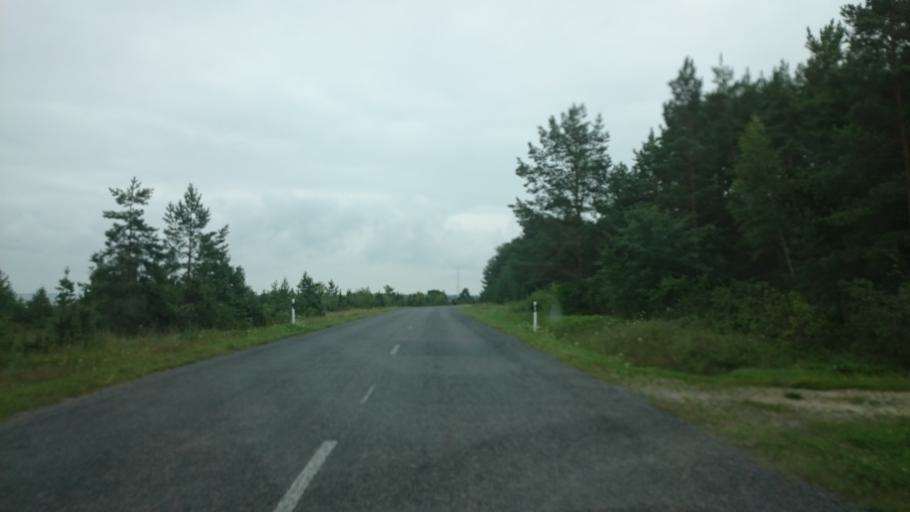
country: EE
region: Saare
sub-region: Orissaare vald
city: Orissaare
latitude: 58.5861
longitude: 23.0233
